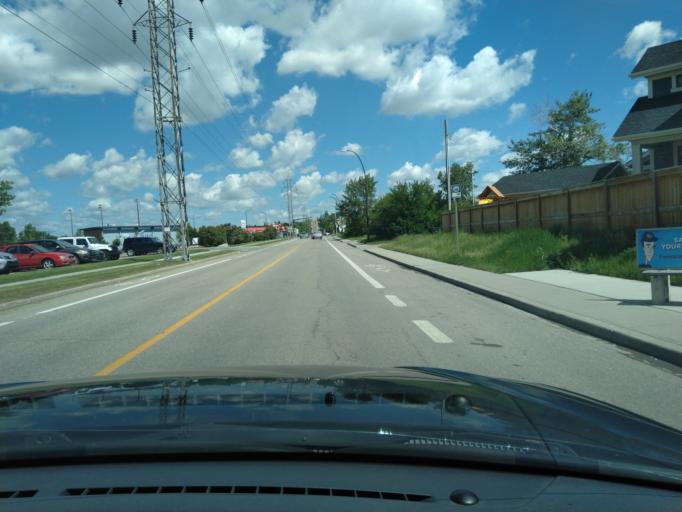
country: CA
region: Alberta
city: Calgary
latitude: 51.0709
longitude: -114.1644
